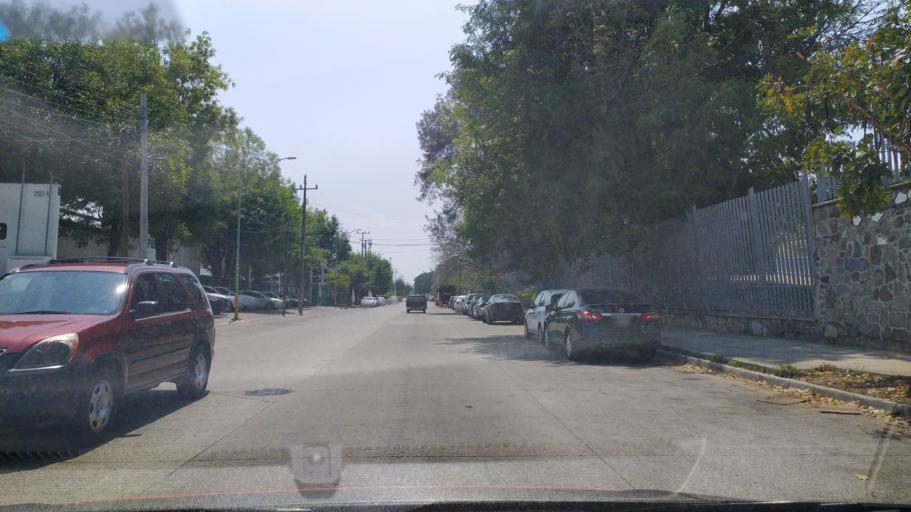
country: MX
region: Jalisco
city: Guadalajara
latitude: 20.6483
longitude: -103.3667
